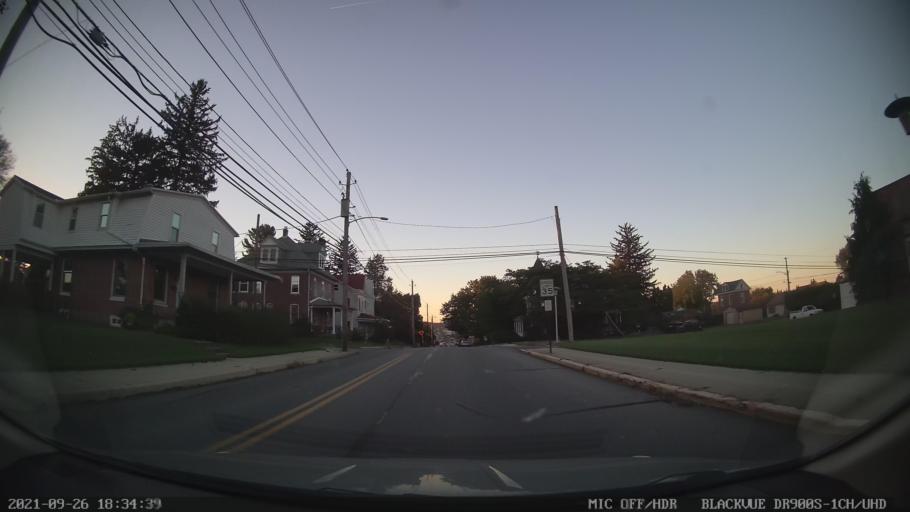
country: US
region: Pennsylvania
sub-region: Berks County
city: Kutztown
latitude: 40.5126
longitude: -75.7735
